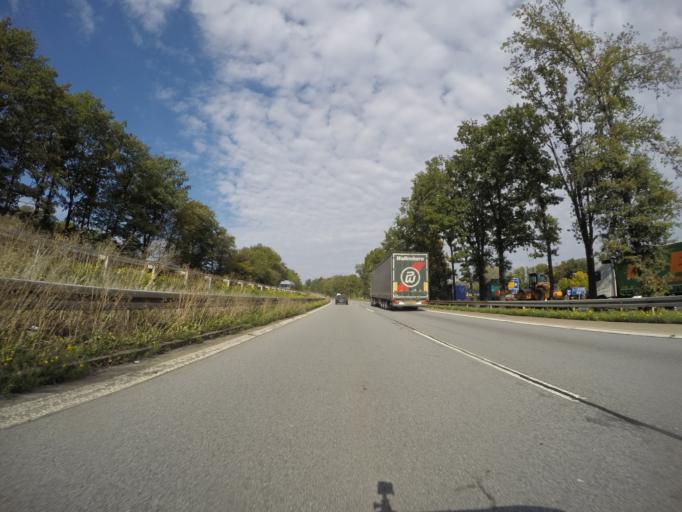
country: DE
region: Bavaria
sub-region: Regierungsbezirk Unterfranken
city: Weibersbrunn
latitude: 49.8984
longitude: 9.3923
